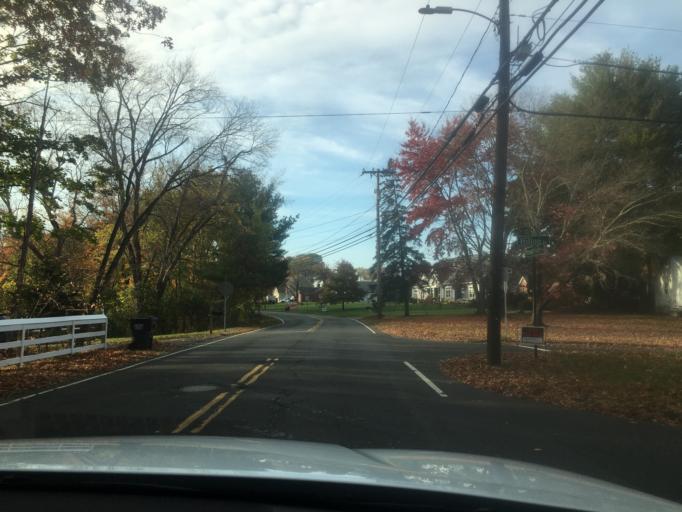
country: US
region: Connecticut
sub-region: Hartford County
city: South Windsor
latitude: 41.8168
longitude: -72.6011
